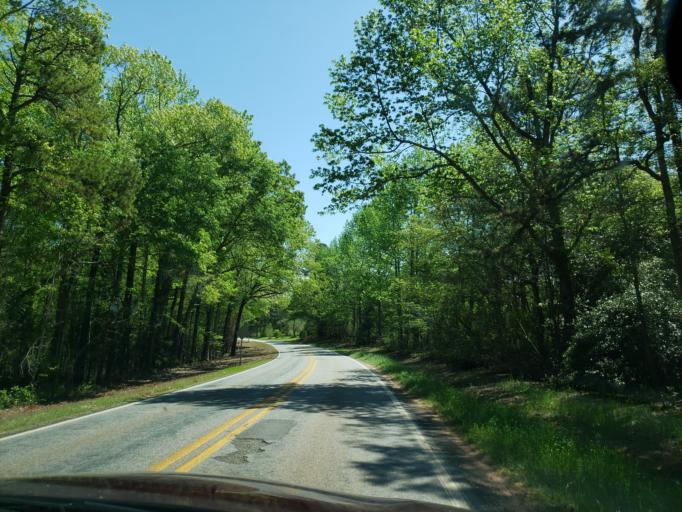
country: US
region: Alabama
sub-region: Tallapoosa County
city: Dadeville
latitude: 32.7075
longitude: -85.8033
